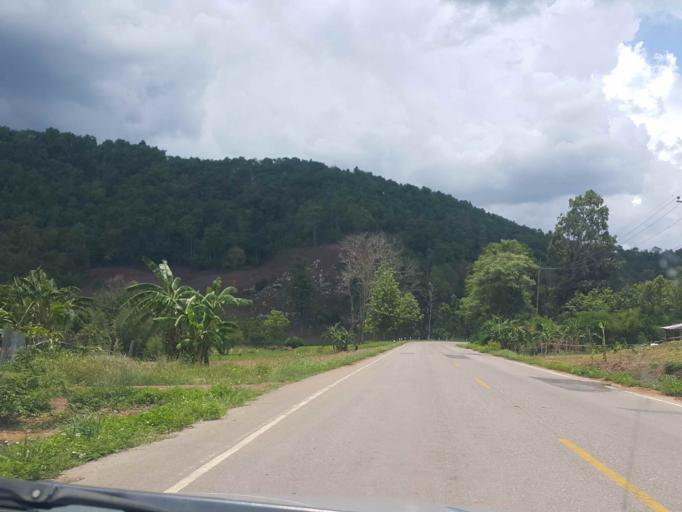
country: TH
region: Phayao
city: Chiang Muan
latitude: 18.8999
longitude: 100.1286
